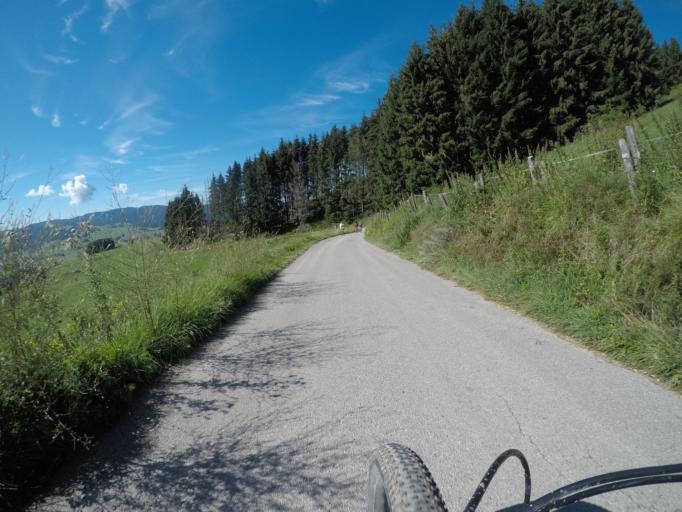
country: IT
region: Veneto
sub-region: Provincia di Vicenza
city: Canove di Roana
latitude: 45.8884
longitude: 11.4844
